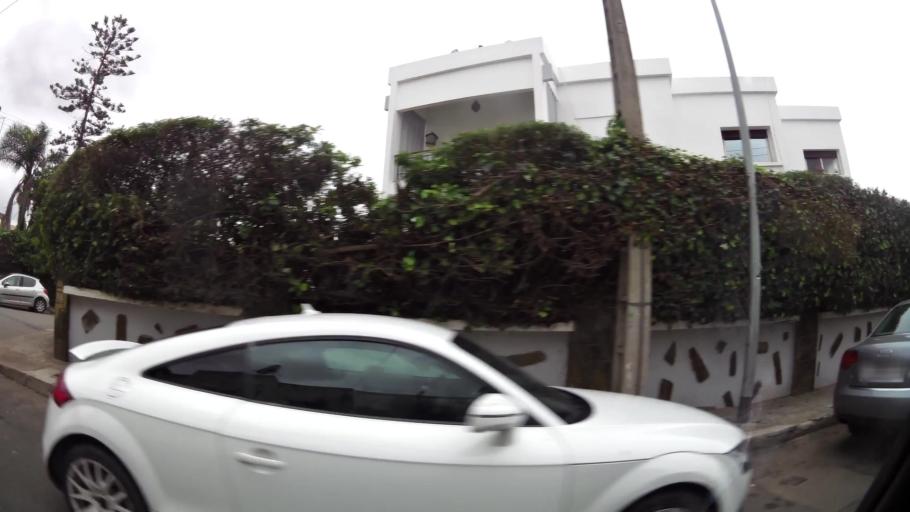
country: MA
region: Grand Casablanca
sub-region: Casablanca
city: Casablanca
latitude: 33.5907
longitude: -7.6496
